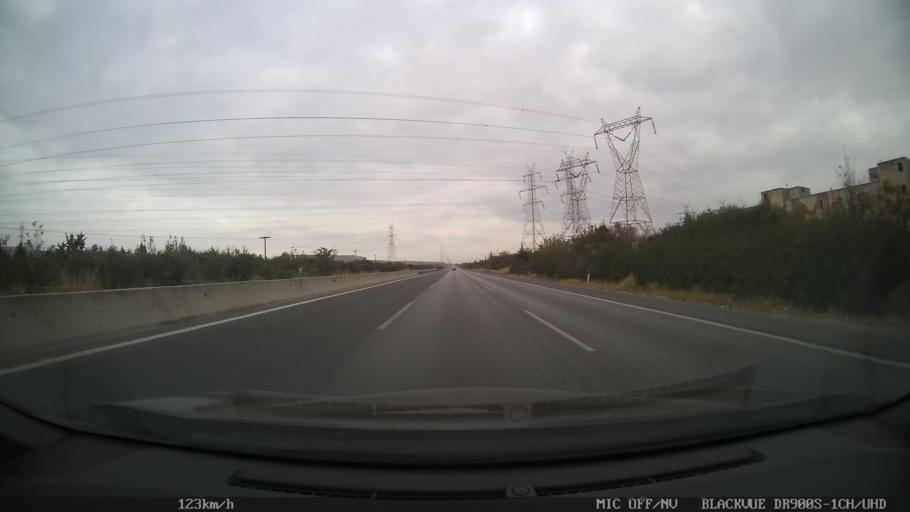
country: GR
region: Central Macedonia
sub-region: Nomos Thessalonikis
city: Evosmos
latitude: 40.6956
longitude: 22.9216
